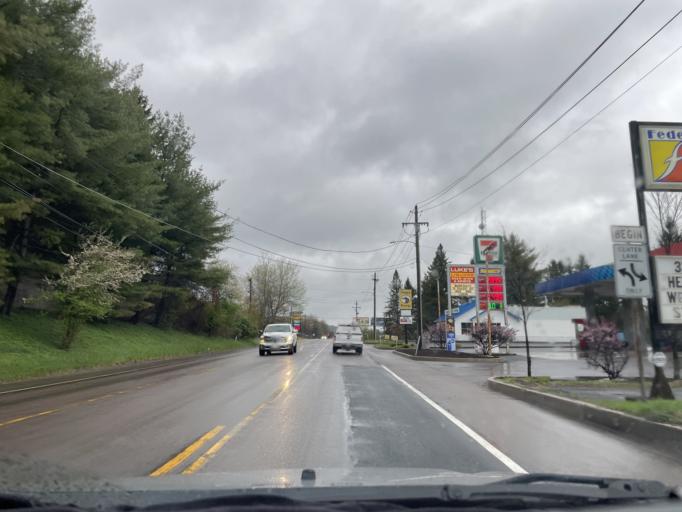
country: US
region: Maryland
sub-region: Garrett County
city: Oakland
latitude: 39.4170
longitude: -79.4017
